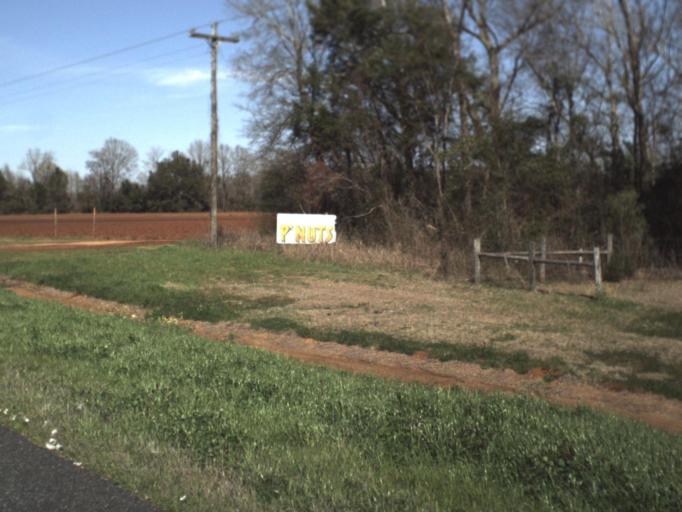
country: US
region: Florida
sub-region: Jackson County
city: Marianna
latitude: 30.8650
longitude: -85.3572
